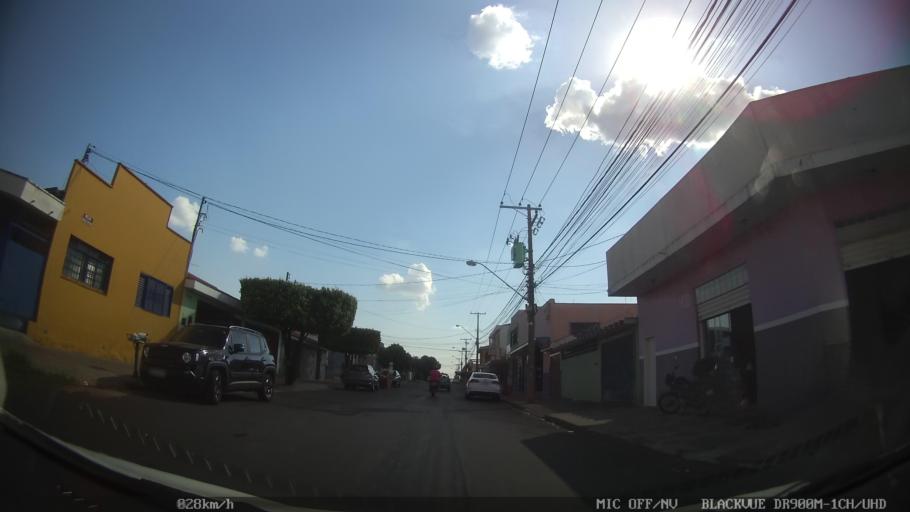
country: BR
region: Sao Paulo
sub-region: Ribeirao Preto
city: Ribeirao Preto
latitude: -21.1833
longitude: -47.8339
